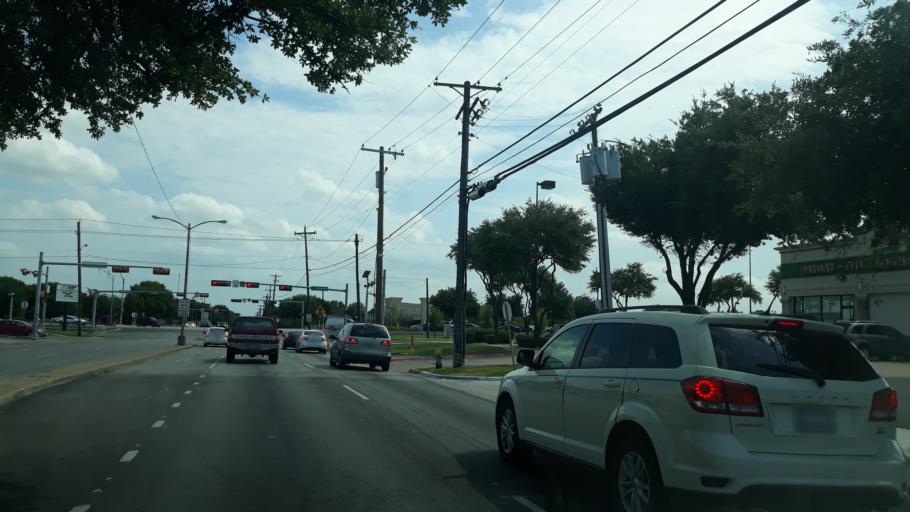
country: US
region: Texas
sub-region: Dallas County
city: Irving
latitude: 32.8297
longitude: -96.9765
